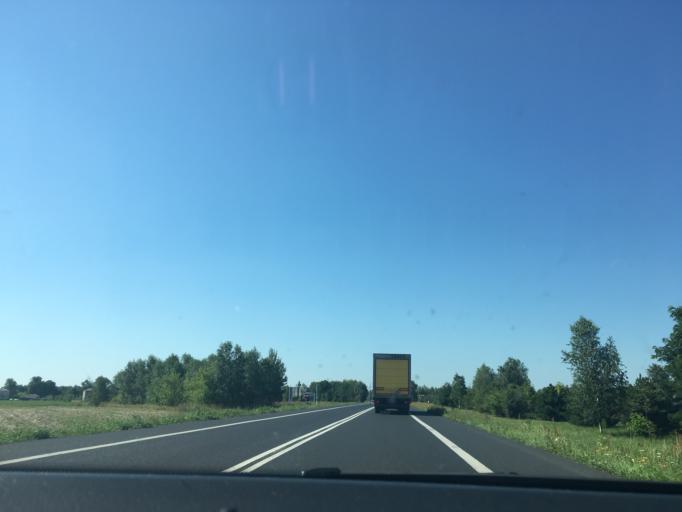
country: PL
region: Lublin Voivodeship
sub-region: Powiat lubartowski
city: Lubartow
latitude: 51.4680
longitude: 22.5805
